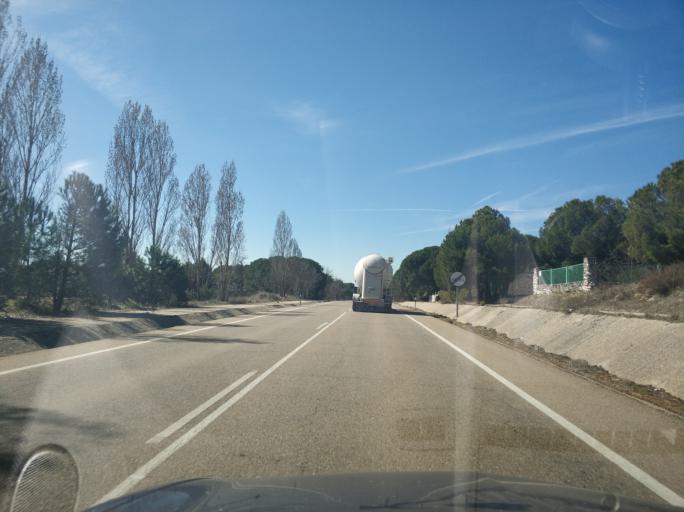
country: ES
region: Castille and Leon
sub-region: Provincia de Valladolid
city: Boecillo
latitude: 41.5448
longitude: -4.6731
